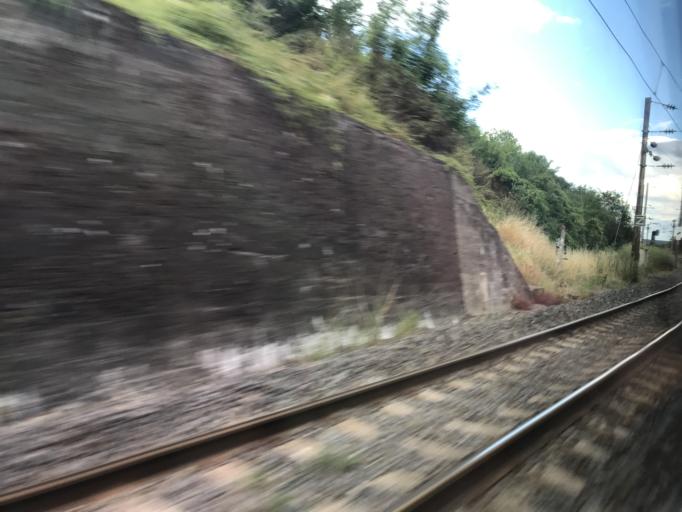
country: FR
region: Lorraine
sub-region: Departement de la Meuse
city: Montmedy
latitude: 49.5229
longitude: 5.3677
